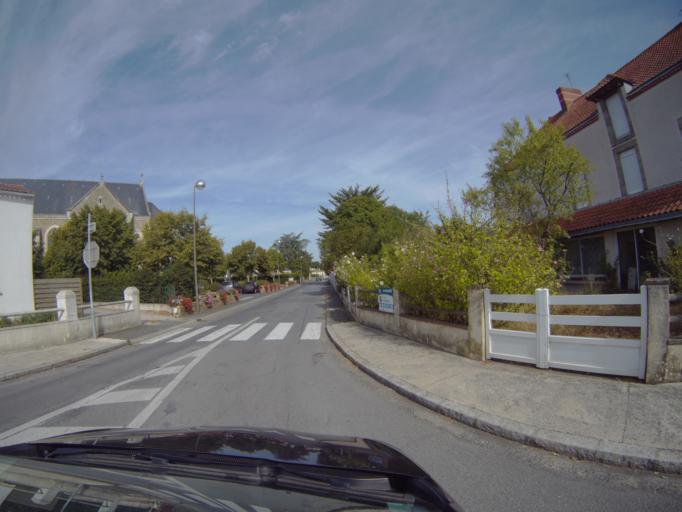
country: FR
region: Pays de la Loire
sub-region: Departement de la Vendee
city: Saint-Andre-Treize-Voies
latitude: 46.9089
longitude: -1.3766
